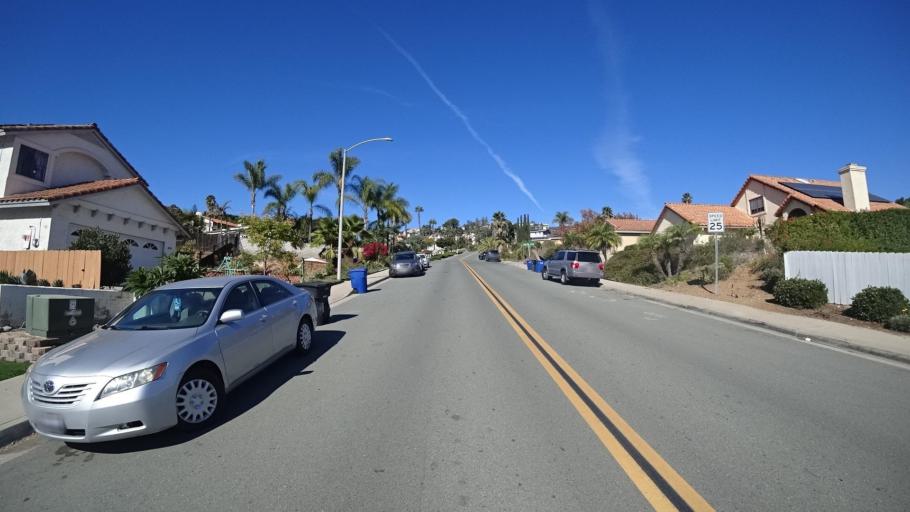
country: US
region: California
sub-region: San Diego County
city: La Presa
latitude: 32.7179
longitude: -116.9794
